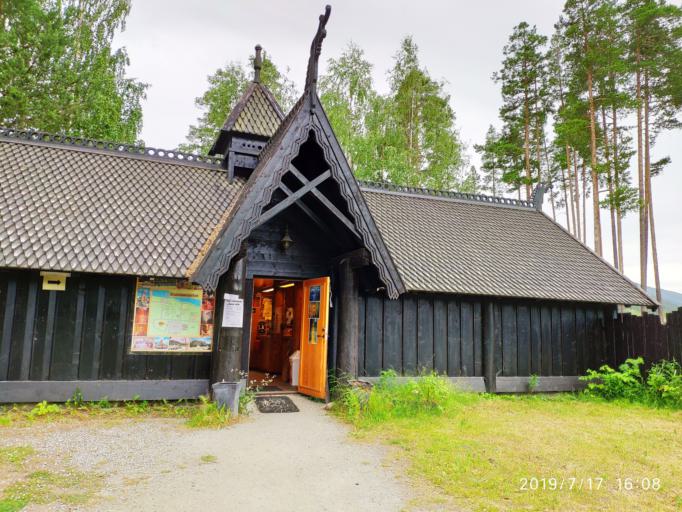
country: NO
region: Buskerud
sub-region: Gol
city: Gol
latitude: 60.6985
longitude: 8.9478
